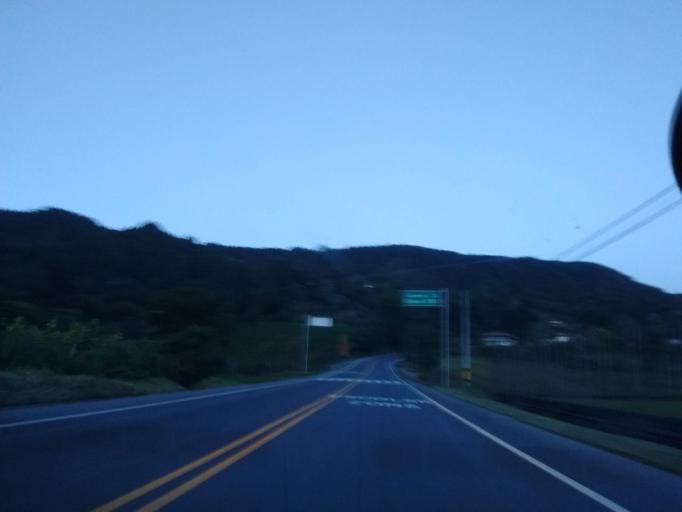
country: CO
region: Antioquia
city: Santuario
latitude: 6.1240
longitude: -75.2399
